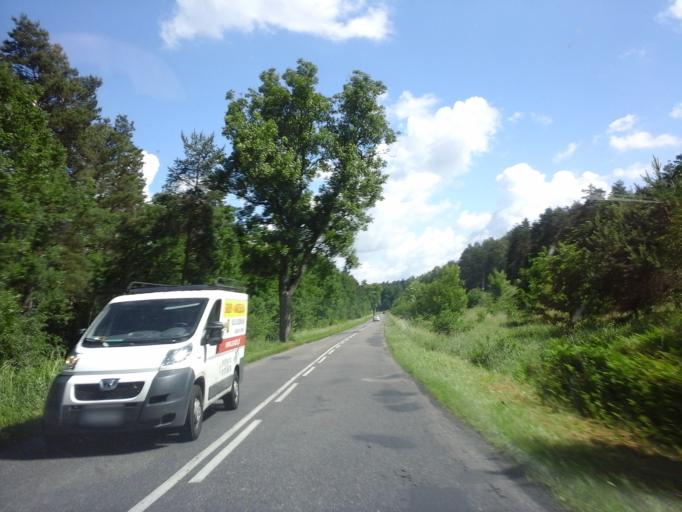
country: PL
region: West Pomeranian Voivodeship
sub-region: Powiat lobeski
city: Lobez
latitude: 53.6625
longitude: 15.6522
